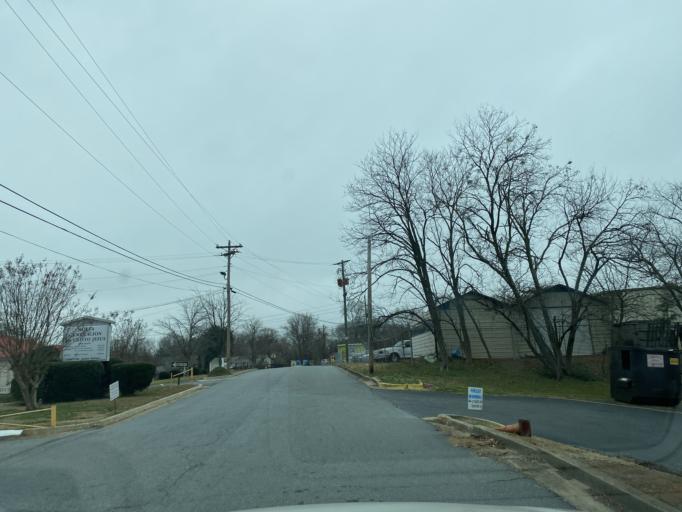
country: US
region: Georgia
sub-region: Cobb County
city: Fair Oaks
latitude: 33.9005
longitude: -84.5687
